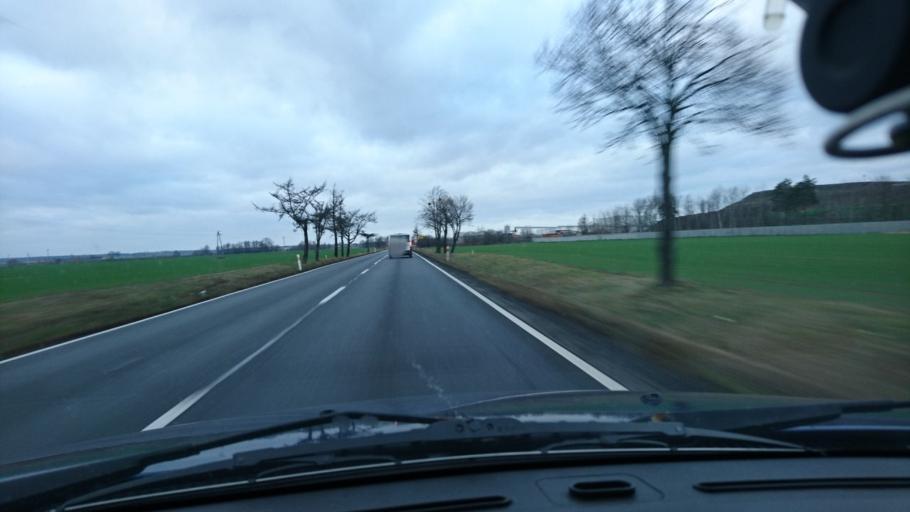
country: PL
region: Opole Voivodeship
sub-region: Powiat kluczborski
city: Kluczbork
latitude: 50.9991
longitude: 18.2068
